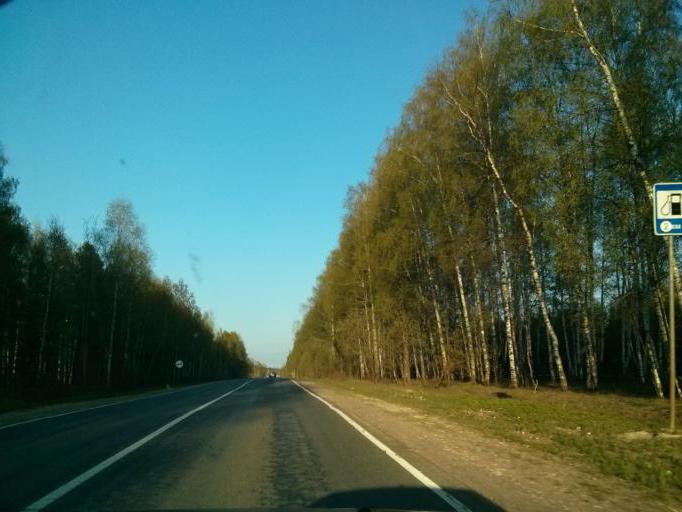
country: RU
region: Nizjnij Novgorod
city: Vacha
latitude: 55.7486
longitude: 42.4728
